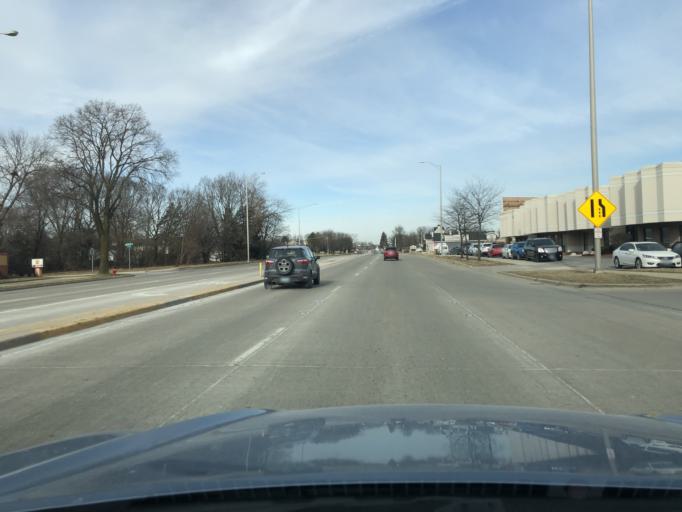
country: US
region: Illinois
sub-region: Cook County
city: Wheeling
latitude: 42.1567
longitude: -87.9163
